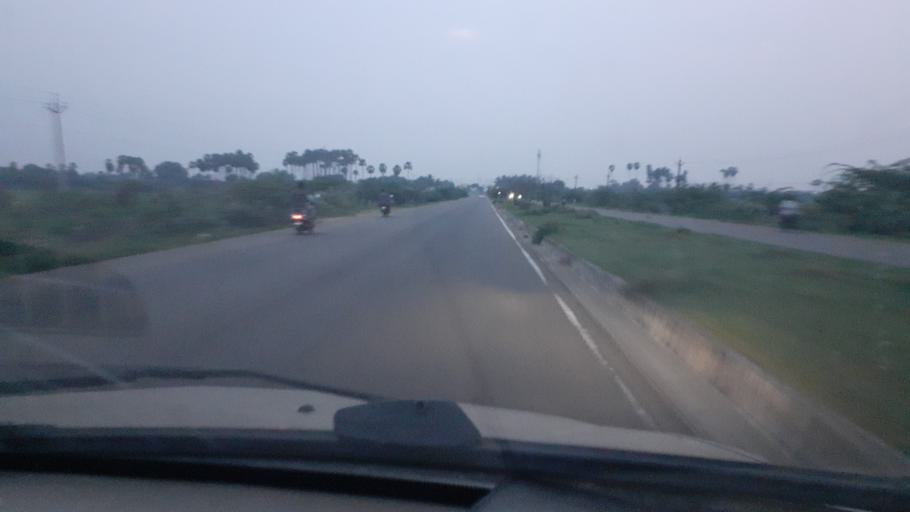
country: IN
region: Tamil Nadu
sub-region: Thoothukkudi
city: Srivaikuntam
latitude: 8.7118
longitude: 77.8279
